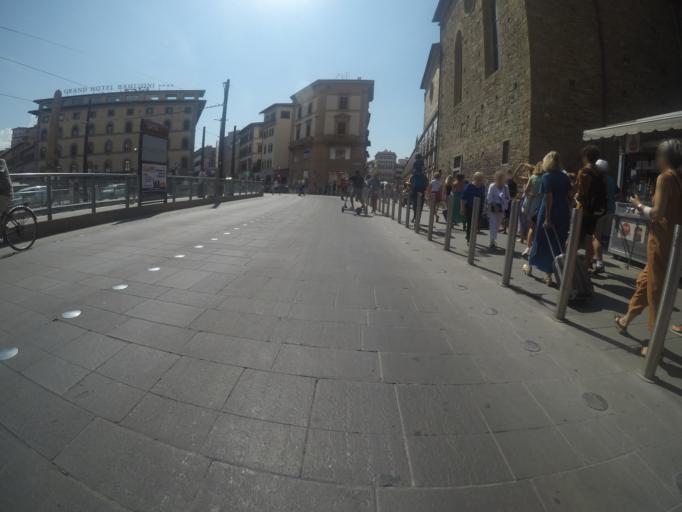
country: IT
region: Tuscany
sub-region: Province of Florence
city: Florence
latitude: 43.7751
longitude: 11.2498
